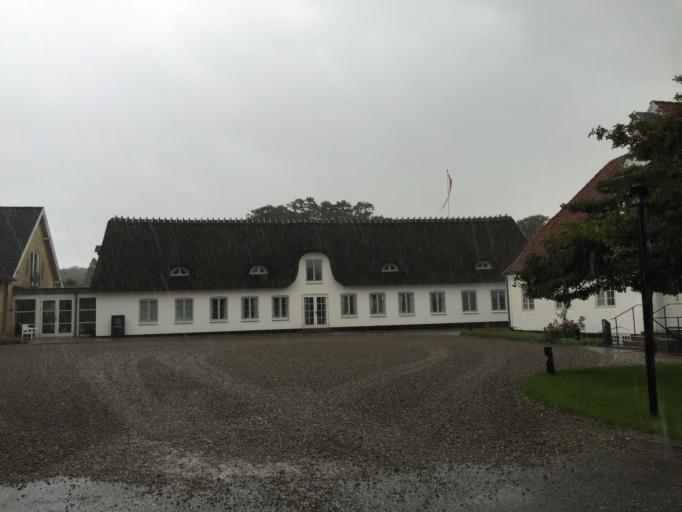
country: DK
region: South Denmark
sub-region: Sonderborg Kommune
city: Dybbol
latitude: 54.9497
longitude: 9.7493
